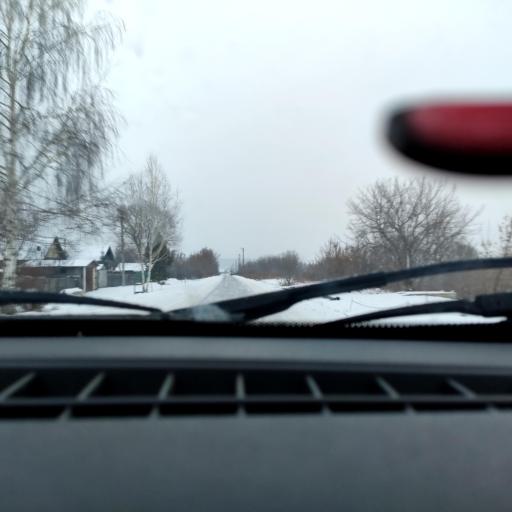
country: RU
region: Bashkortostan
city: Blagoveshchensk
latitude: 54.9007
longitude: 56.0163
